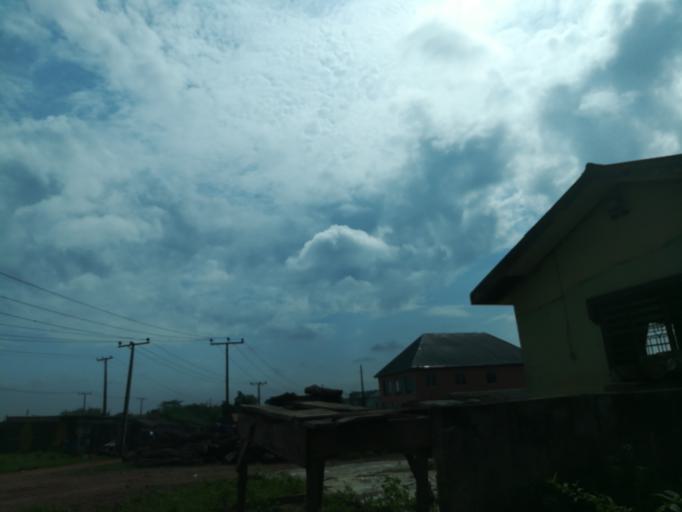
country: NG
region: Lagos
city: Ikorodu
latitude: 6.6312
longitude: 3.5303
